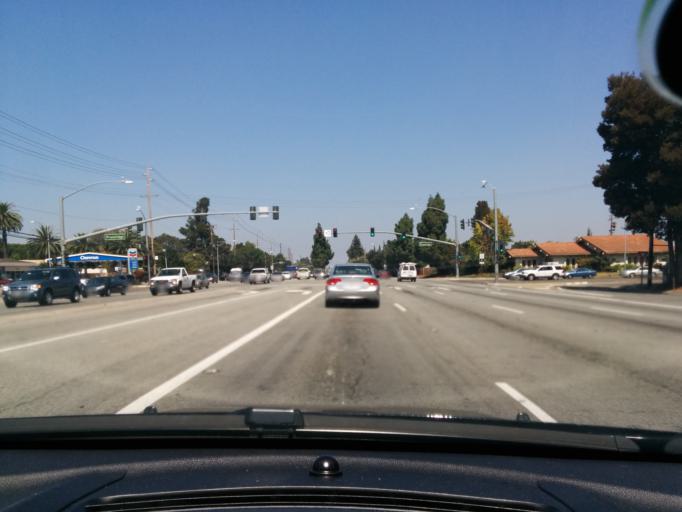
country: US
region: California
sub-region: Santa Clara County
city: Cupertino
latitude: 37.3307
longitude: -121.9955
